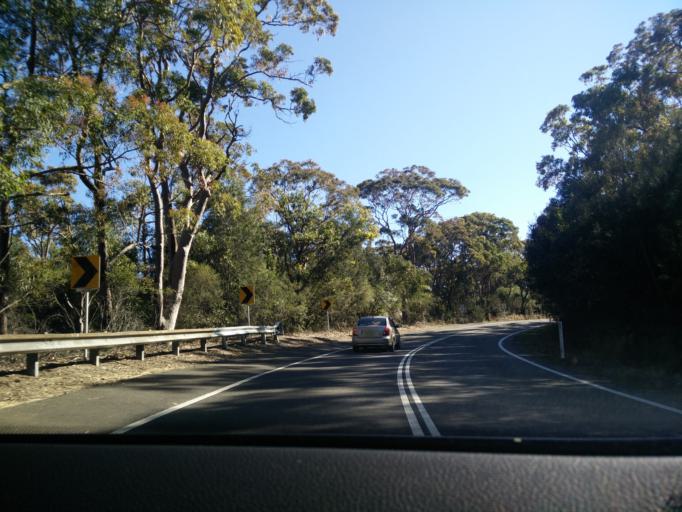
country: AU
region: New South Wales
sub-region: Hornsby Shire
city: Berowra
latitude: -33.5999
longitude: 151.1645
